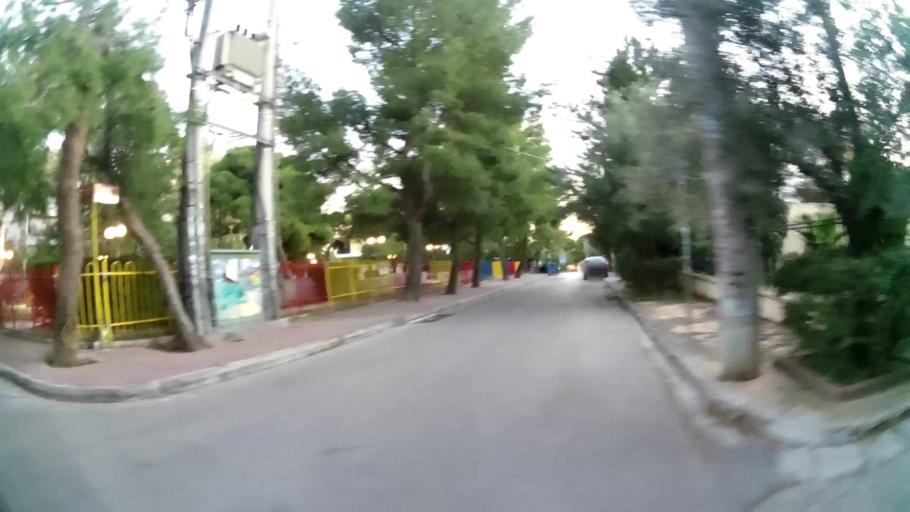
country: GR
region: Attica
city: Pefki
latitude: 38.0666
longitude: 23.8010
